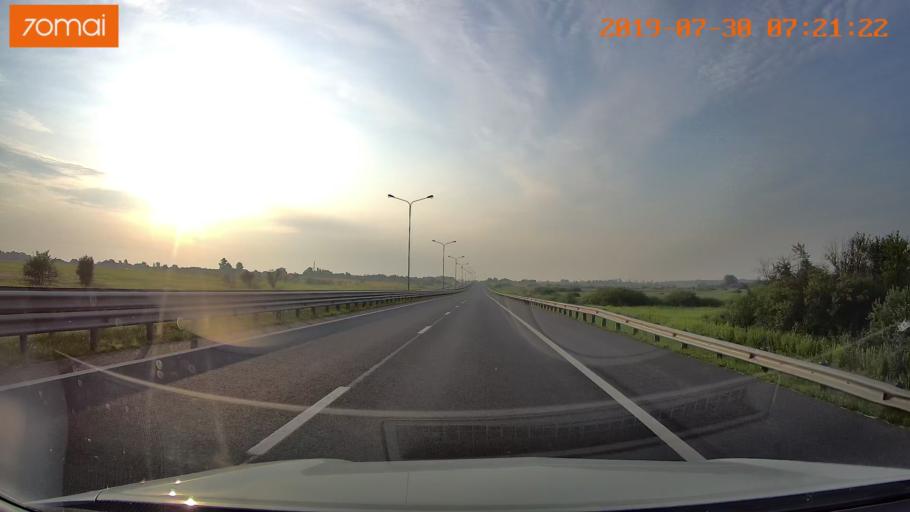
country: RU
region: Kaliningrad
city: Bol'shoe Isakovo
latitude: 54.6966
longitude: 20.7271
